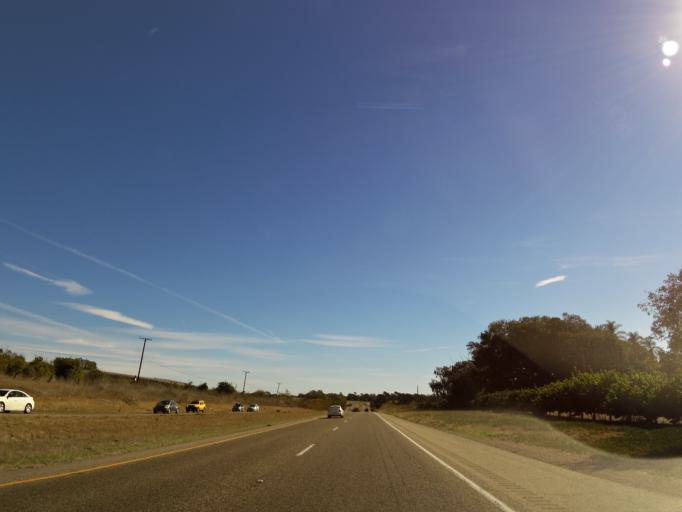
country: US
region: California
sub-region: Santa Barbara County
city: Isla Vista
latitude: 34.4516
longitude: -119.9648
